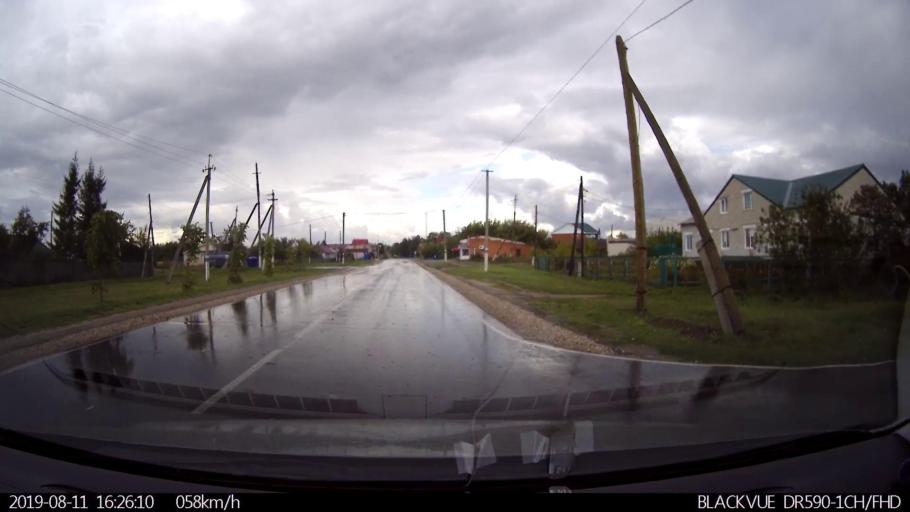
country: RU
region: Ulyanovsk
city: Mayna
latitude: 54.1091
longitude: 47.6134
